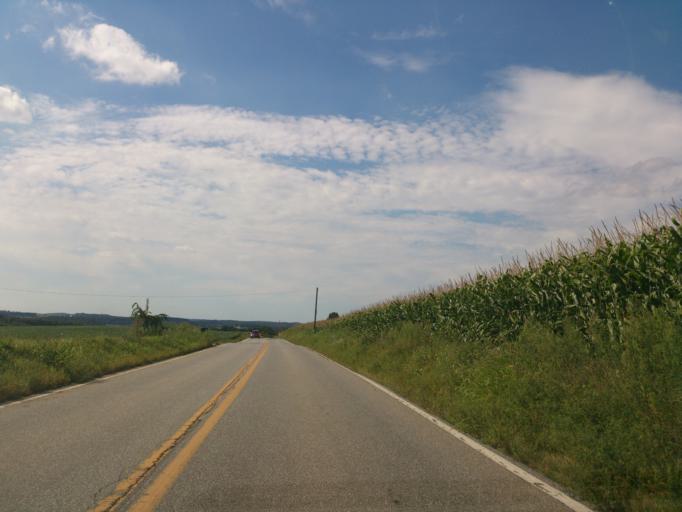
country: US
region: Pennsylvania
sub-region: York County
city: Susquehanna Trails
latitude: 39.7808
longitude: -76.4674
